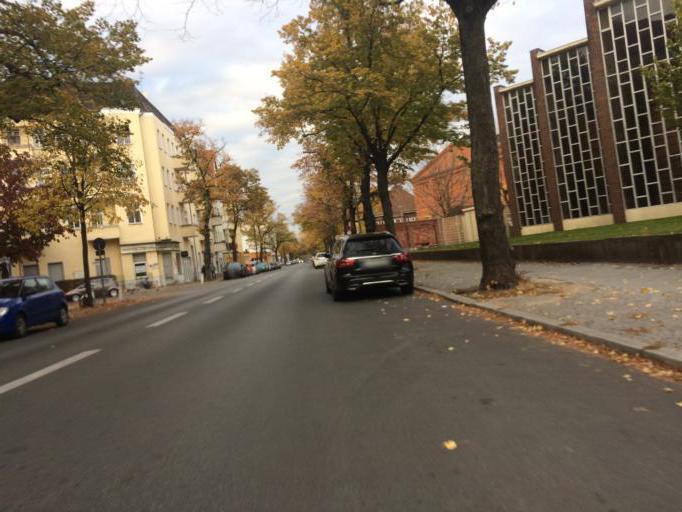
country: DE
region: Berlin
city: Gesundbrunnen
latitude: 52.5669
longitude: 13.3787
